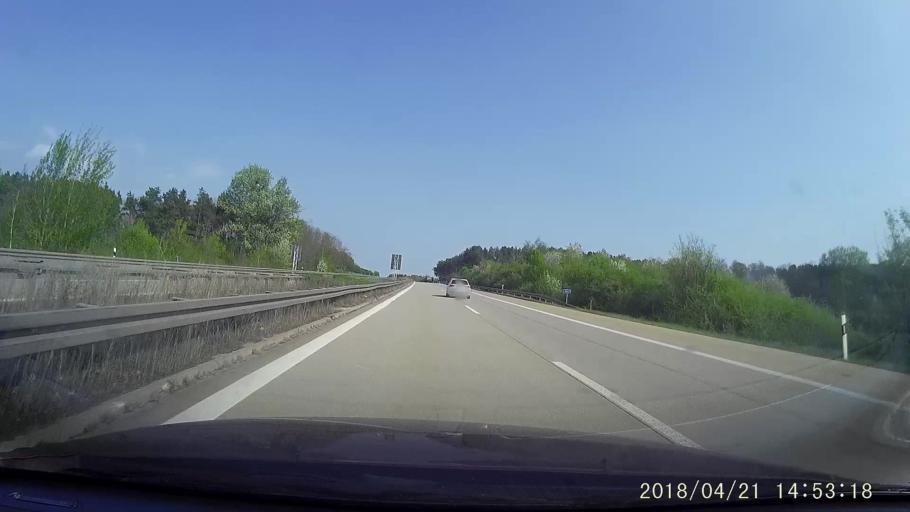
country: DE
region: Saxony
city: Guttau
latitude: 51.2100
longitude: 14.5790
